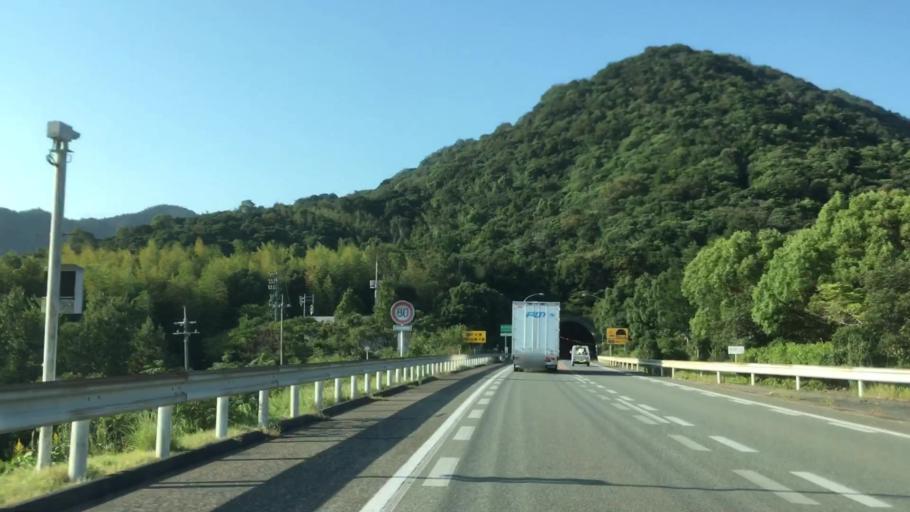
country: JP
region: Yamaguchi
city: Ogori-shimogo
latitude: 34.0993
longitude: 131.4514
